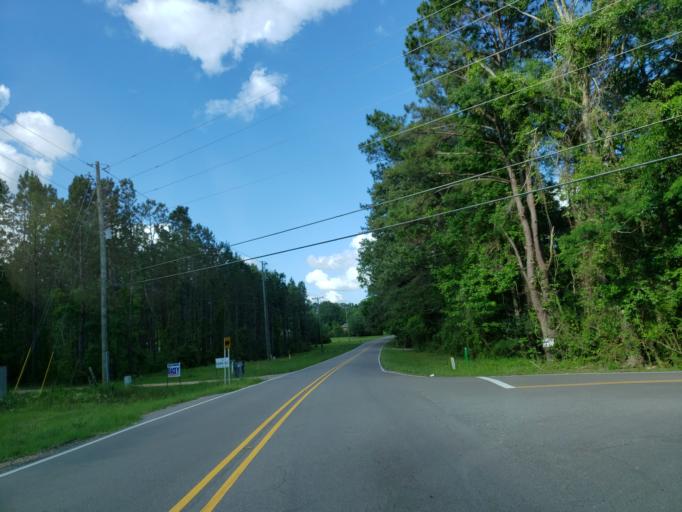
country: US
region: Mississippi
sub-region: Lamar County
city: West Hattiesburg
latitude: 31.2820
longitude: -89.4287
